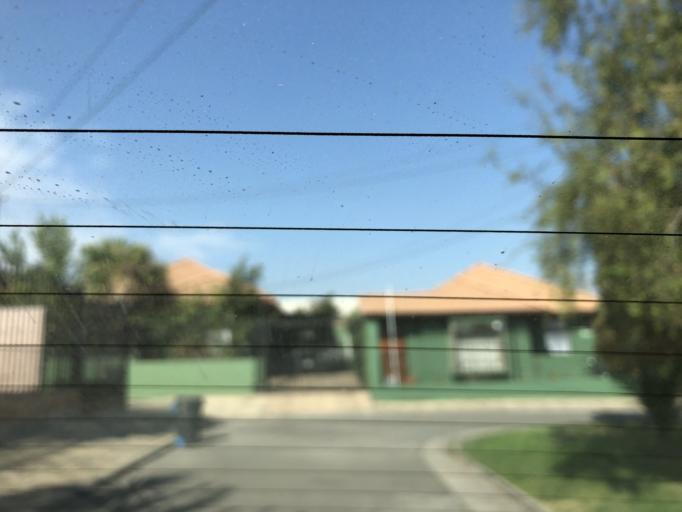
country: CL
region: Santiago Metropolitan
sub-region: Provincia de Cordillera
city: Puente Alto
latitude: -33.5718
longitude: -70.5455
